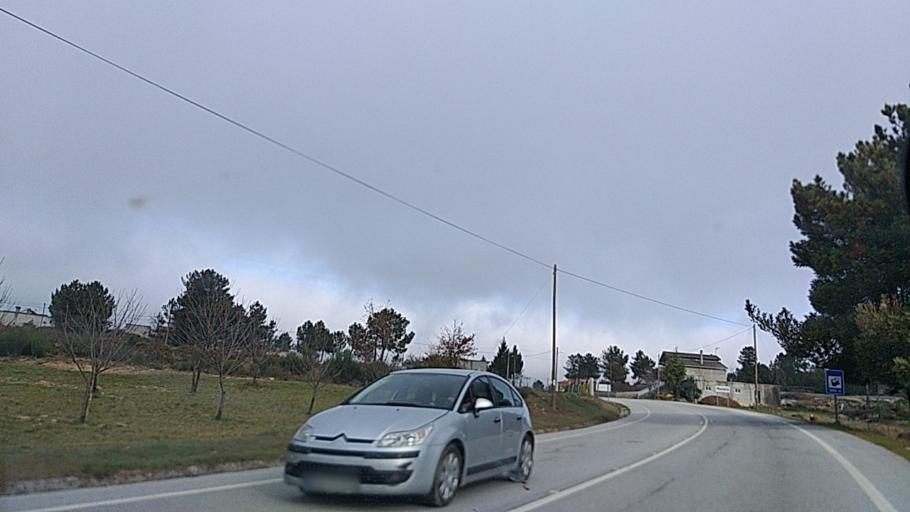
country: PT
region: Guarda
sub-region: Aguiar da Beira
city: Aguiar da Beira
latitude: 40.7381
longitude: -7.4938
